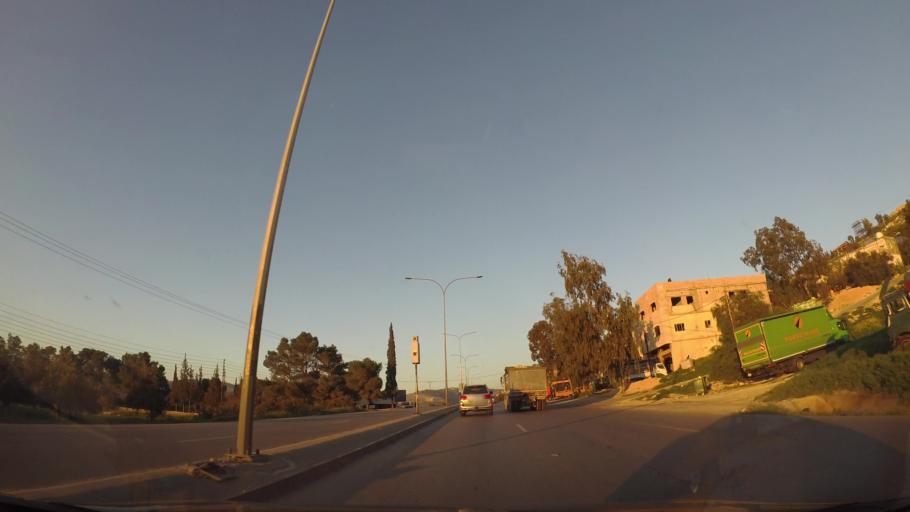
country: JO
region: Amman
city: Umm as Summaq
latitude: 31.8758
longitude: 35.7786
